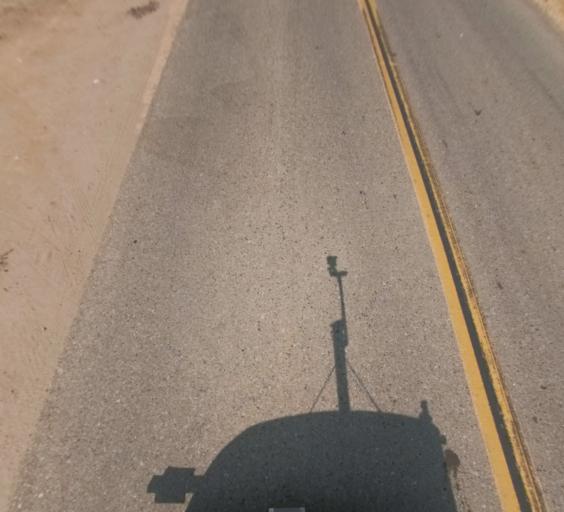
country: US
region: California
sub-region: Madera County
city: Fairmead
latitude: 37.0802
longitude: -120.2018
